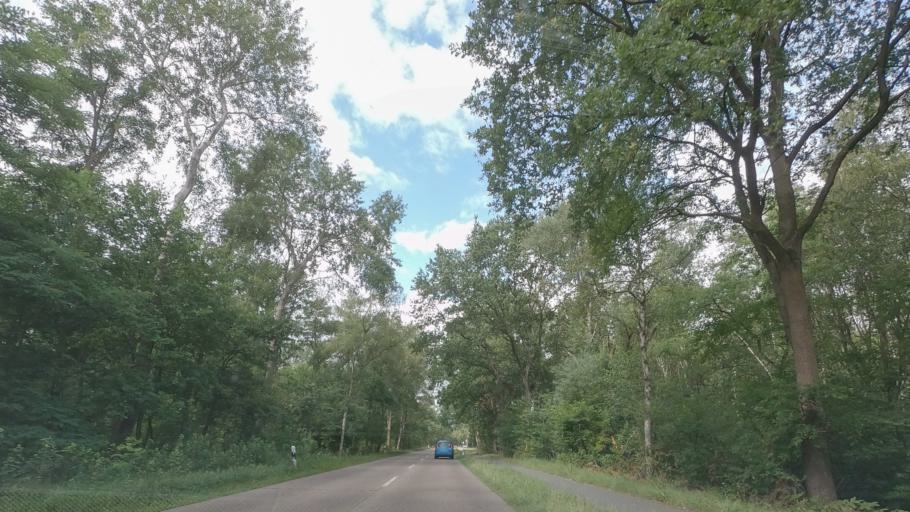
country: DE
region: Lower Saxony
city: Schwanewede
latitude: 53.2310
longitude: 8.5702
